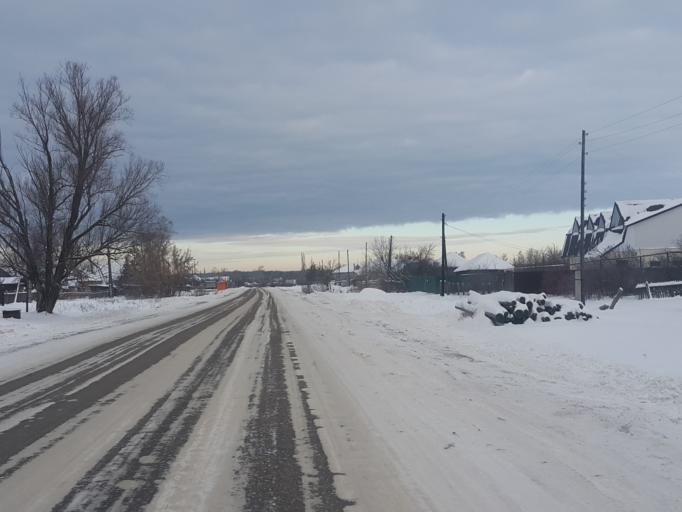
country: RU
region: Tambov
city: Platonovka
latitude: 52.8381
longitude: 41.8139
